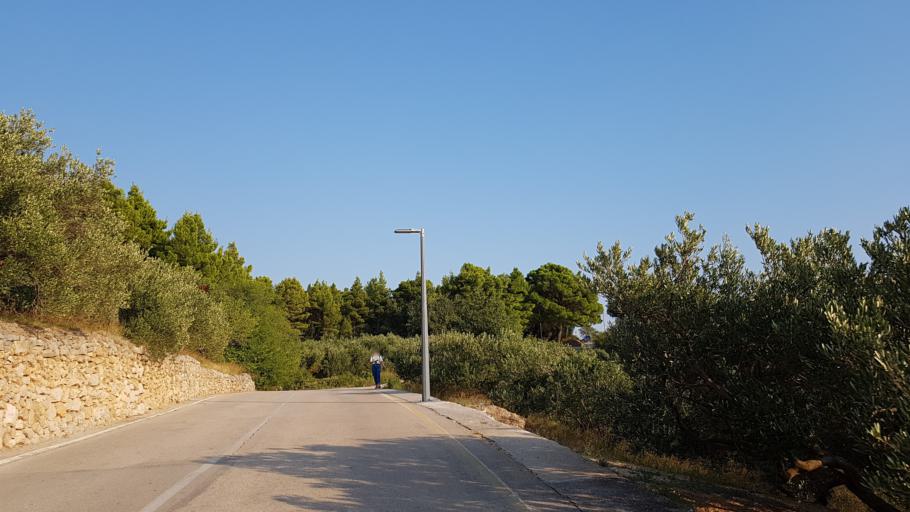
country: HR
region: Splitsko-Dalmatinska
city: Donja Brela
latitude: 43.3816
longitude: 16.9180
